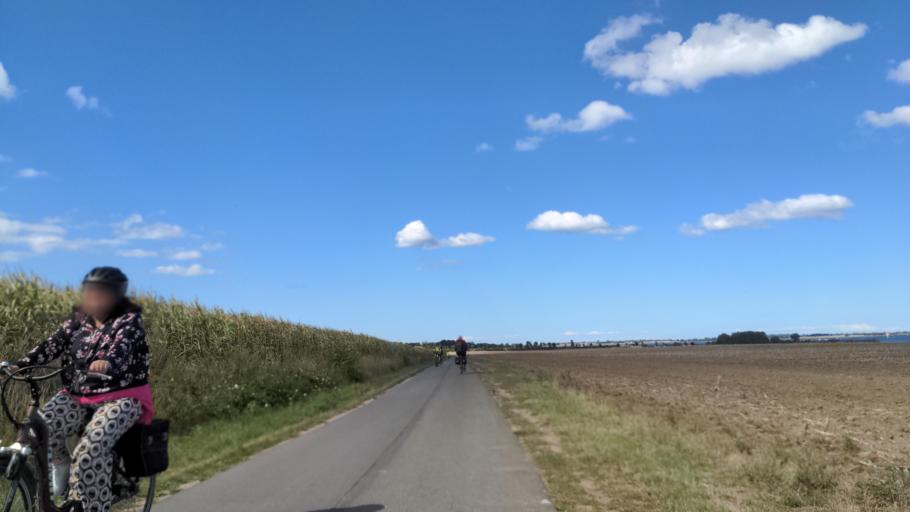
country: DE
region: Mecklenburg-Vorpommern
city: Wismar
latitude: 53.9175
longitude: 11.3993
